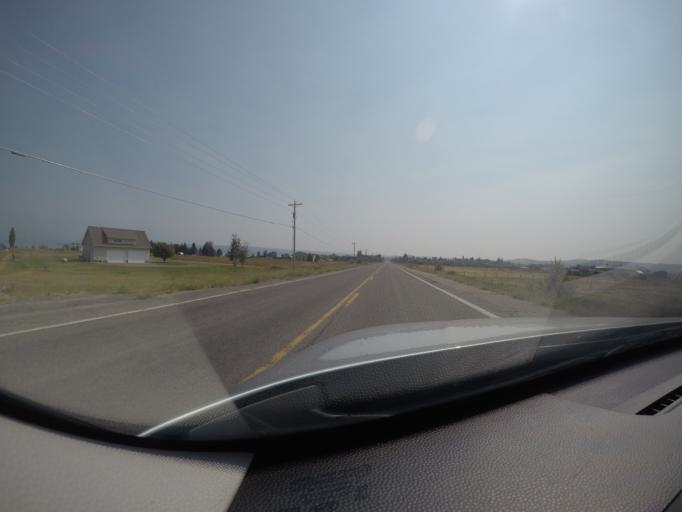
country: US
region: Montana
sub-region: Lake County
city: Polson
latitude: 47.7320
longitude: -114.1887
